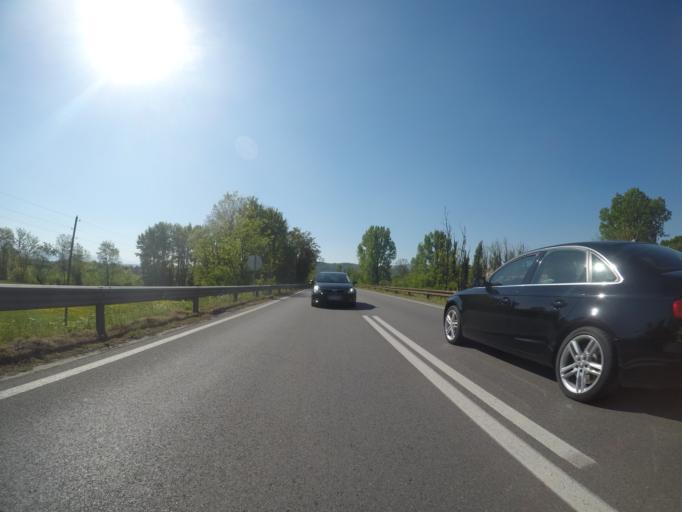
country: ME
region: Danilovgrad
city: Danilovgrad
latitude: 42.5213
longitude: 19.1208
